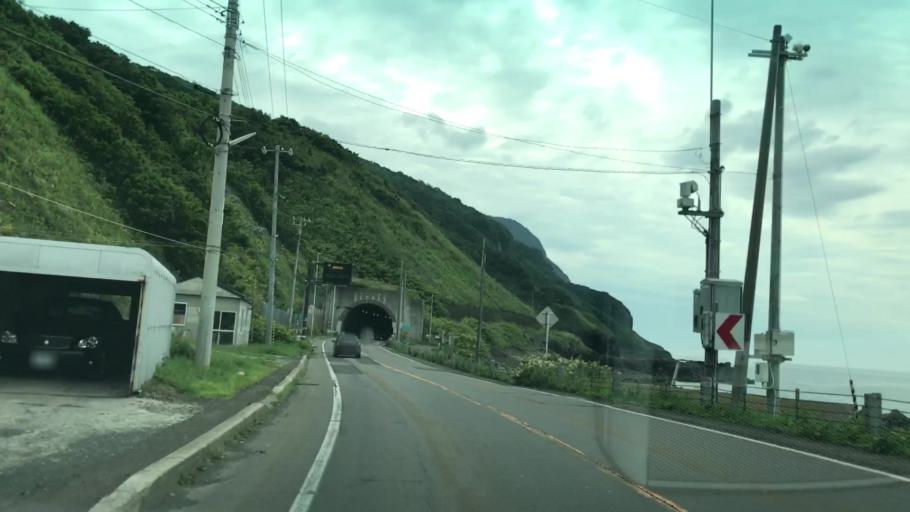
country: JP
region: Hokkaido
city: Iwanai
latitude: 42.9621
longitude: 140.4633
